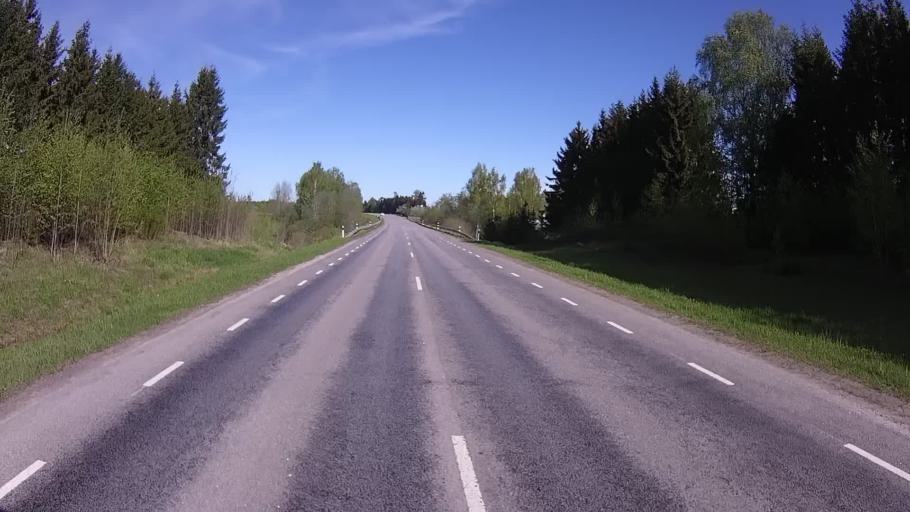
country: EE
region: Polvamaa
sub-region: Polva linn
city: Polva
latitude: 58.2388
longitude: 27.0148
